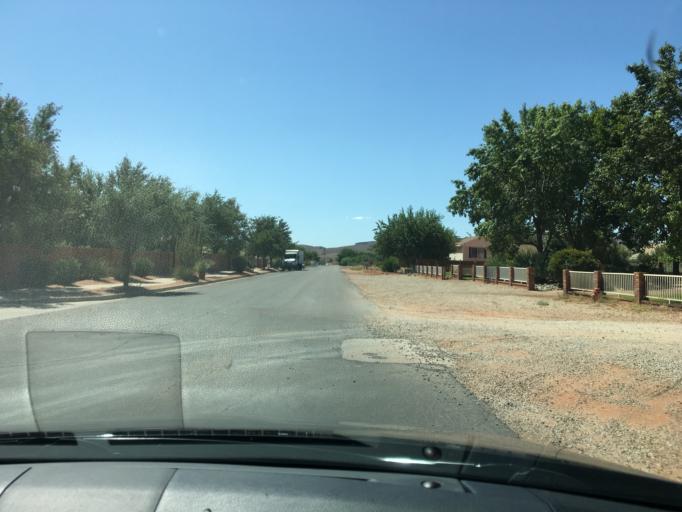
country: US
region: Utah
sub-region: Washington County
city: Ivins
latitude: 37.1641
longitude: -113.6887
